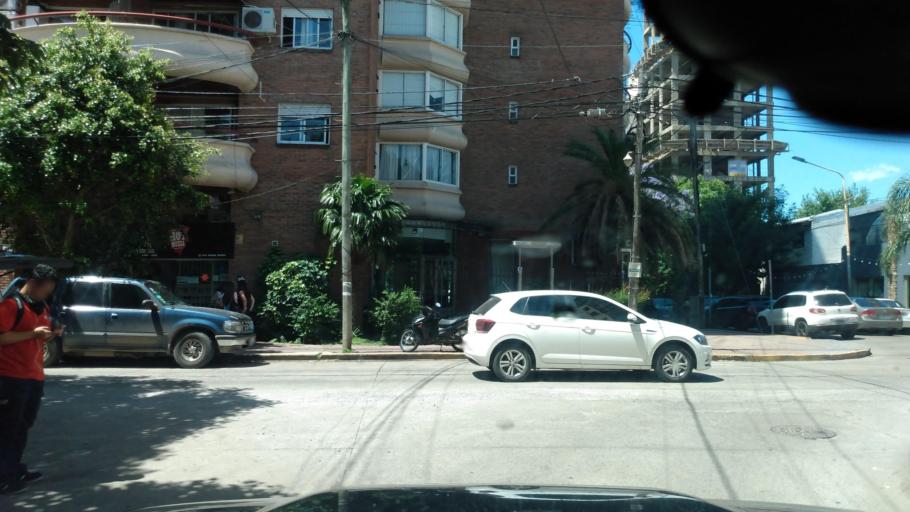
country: AR
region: Buenos Aires
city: Hurlingham
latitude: -34.5415
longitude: -58.7054
